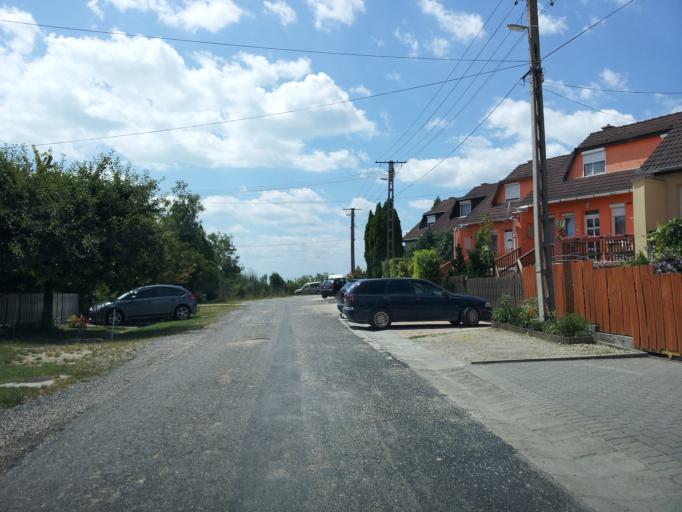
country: HU
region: Veszprem
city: Balatonkenese
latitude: 47.0361
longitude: 18.1197
